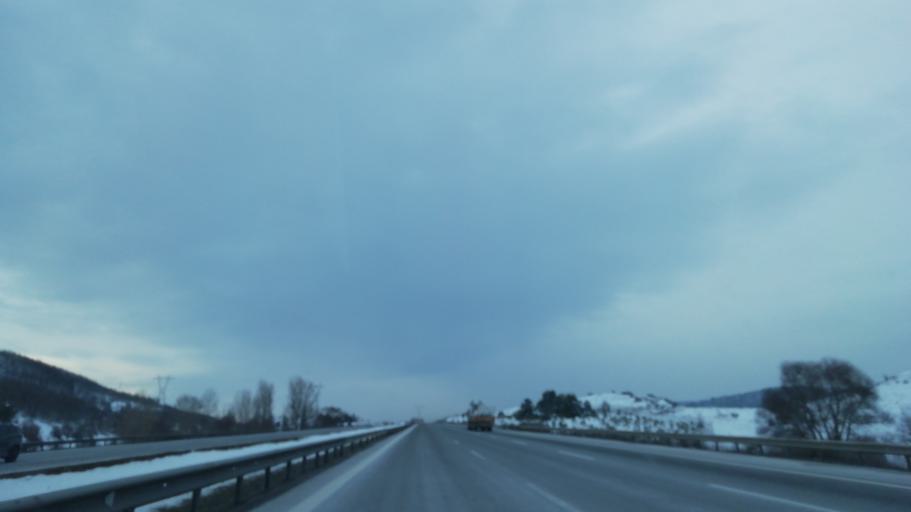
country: TR
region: Bolu
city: Yenicaga
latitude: 40.7620
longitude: 31.9886
